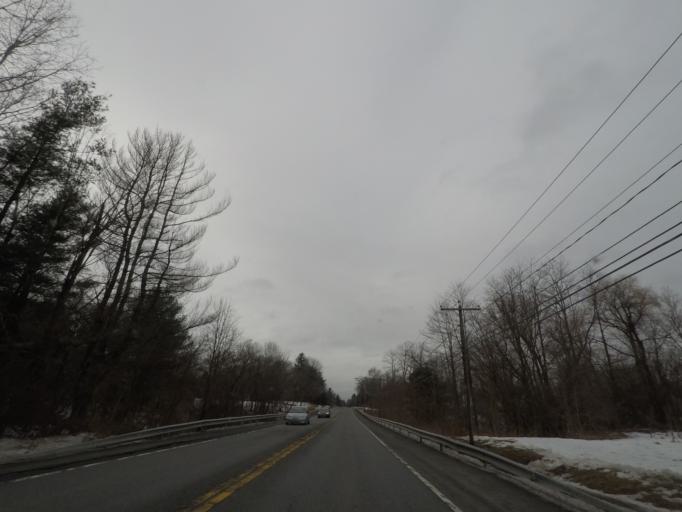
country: US
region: New York
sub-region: Albany County
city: Voorheesville
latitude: 42.7212
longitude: -73.9476
